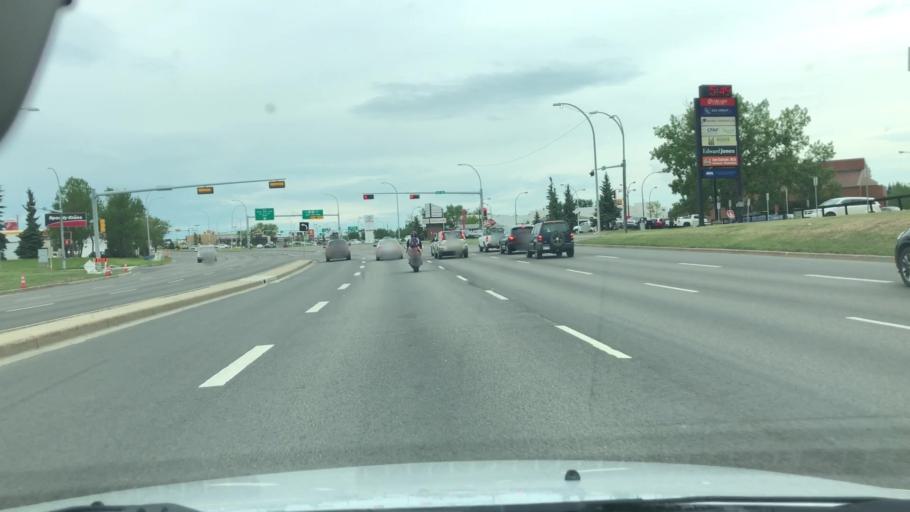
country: CA
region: Alberta
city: St. Albert
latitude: 53.5460
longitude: -113.6158
